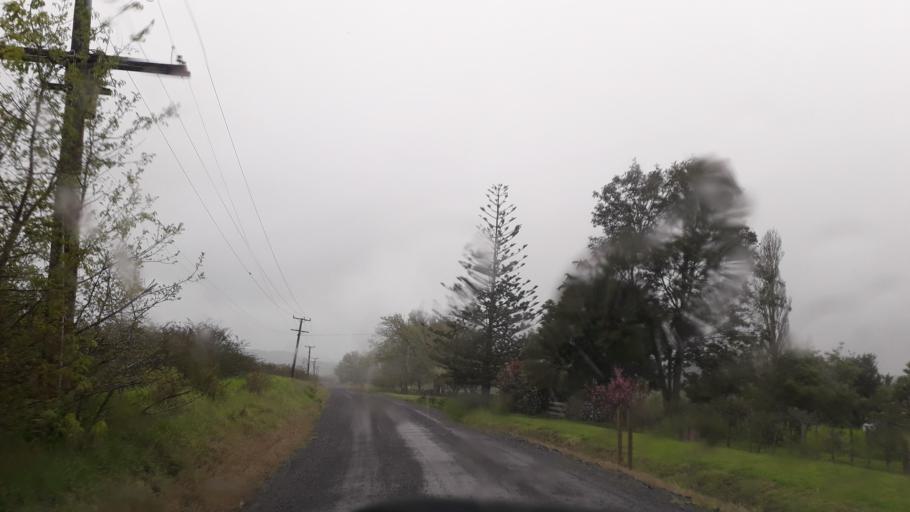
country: NZ
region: Northland
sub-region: Far North District
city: Waimate North
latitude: -35.4827
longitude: 173.6987
